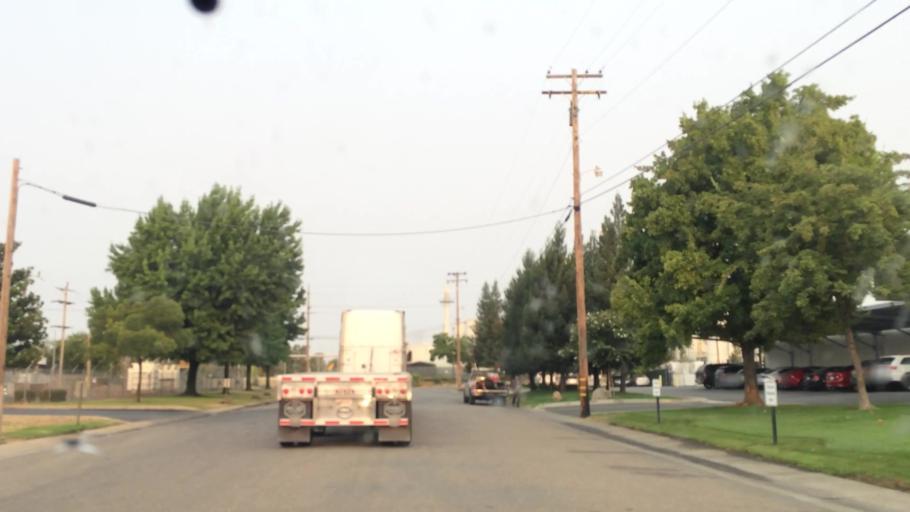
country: US
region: California
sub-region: Sacramento County
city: Florin
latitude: 38.5302
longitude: -121.3977
